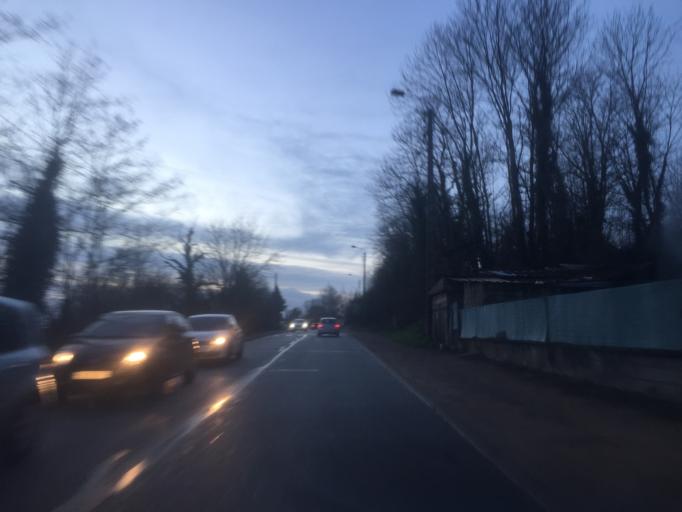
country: FR
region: Franche-Comte
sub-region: Departement du Jura
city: Orchamps
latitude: 47.1477
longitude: 5.6498
